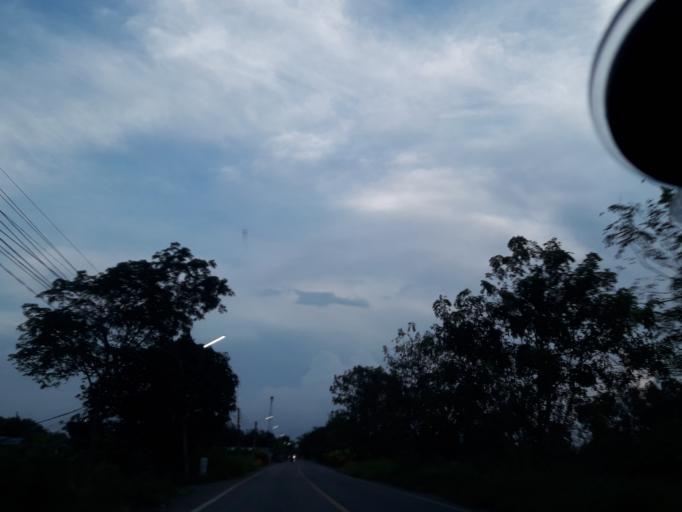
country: TH
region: Pathum Thani
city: Nong Suea
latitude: 14.1236
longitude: 100.8690
